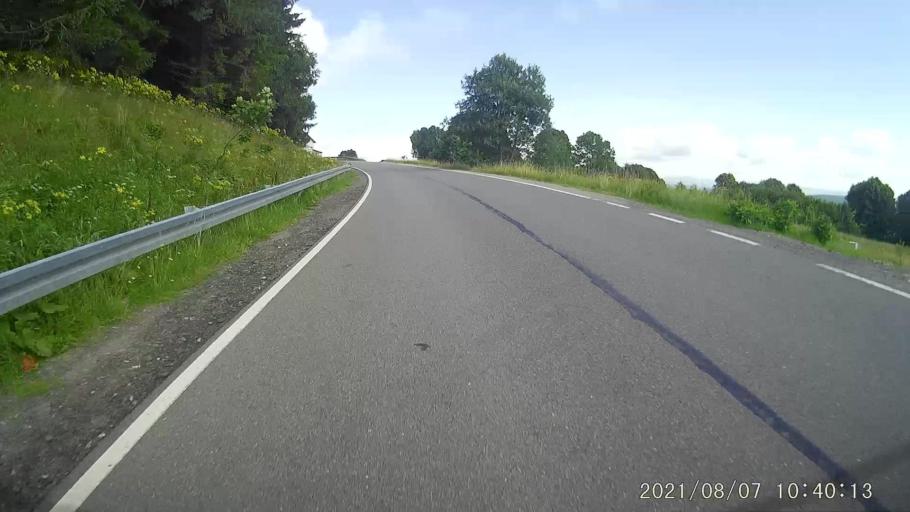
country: PL
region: Lower Silesian Voivodeship
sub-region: Powiat klodzki
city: Duszniki-Zdroj
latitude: 50.3458
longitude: 16.3831
